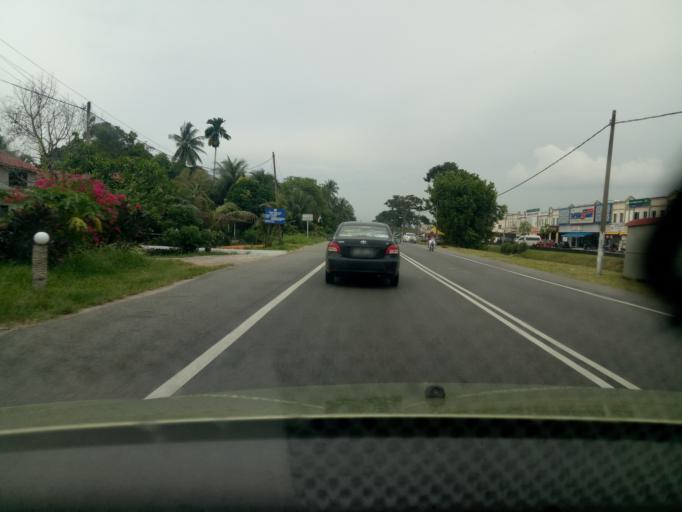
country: MY
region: Kedah
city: Gurun
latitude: 5.8773
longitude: 100.4489
